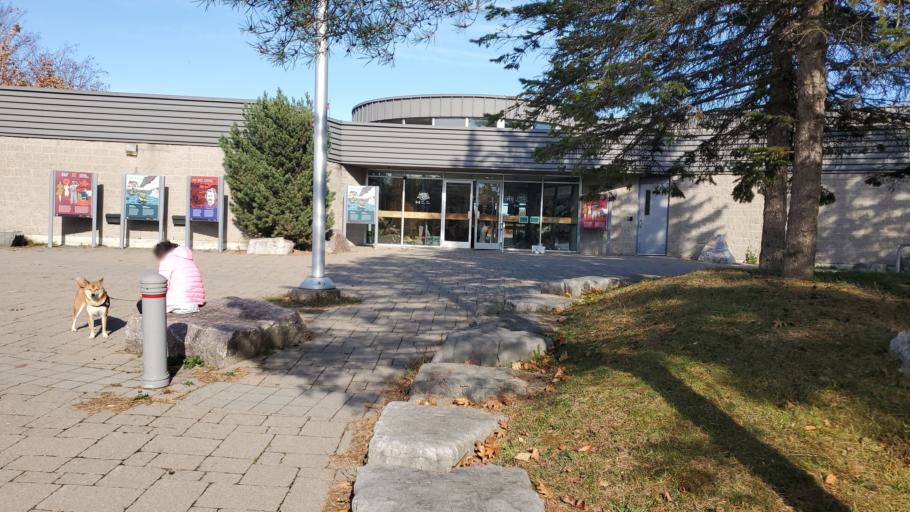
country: CA
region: Ontario
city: Peterborough
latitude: 44.3067
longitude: -78.3018
